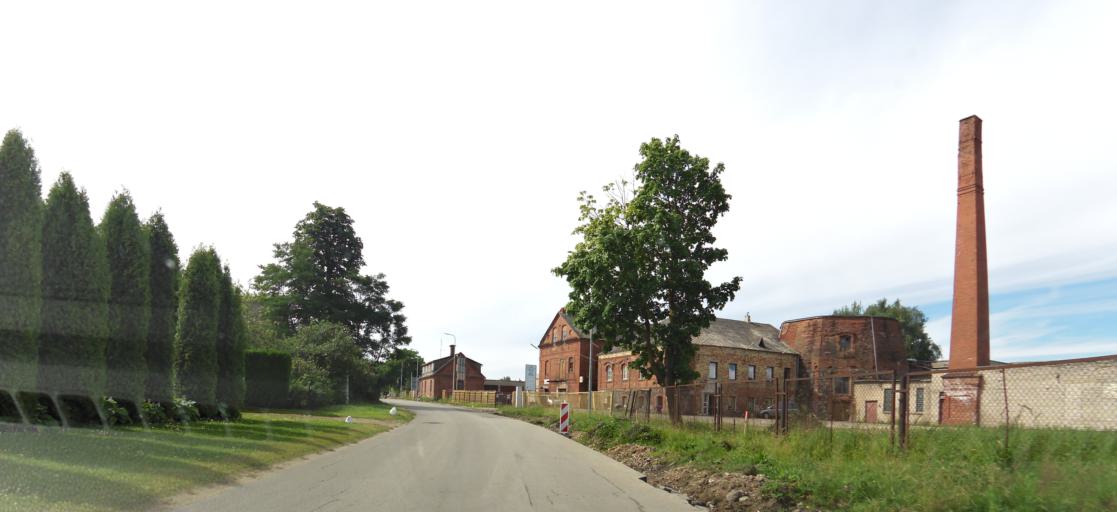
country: LT
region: Panevezys
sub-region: Birzai
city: Birzai
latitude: 56.2078
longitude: 24.7672
